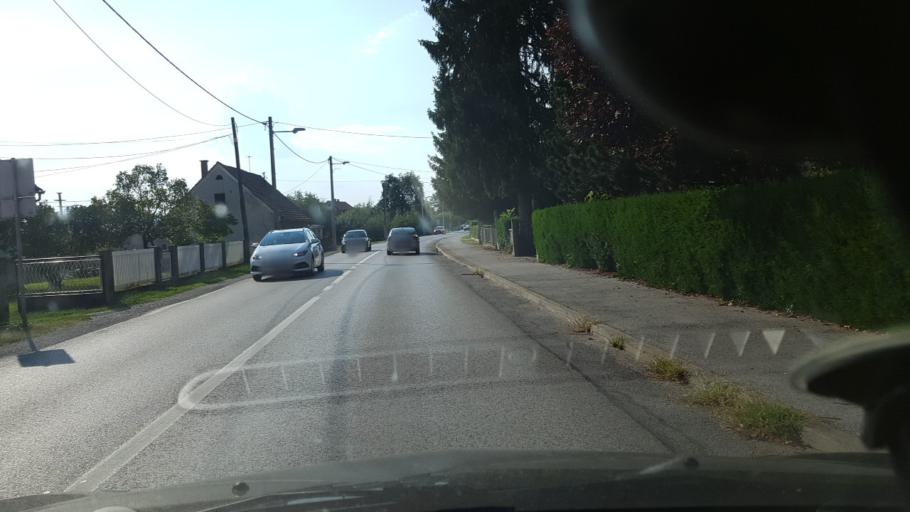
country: HR
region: Zagrebacka
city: Brdovec
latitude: 45.8676
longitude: 15.7600
